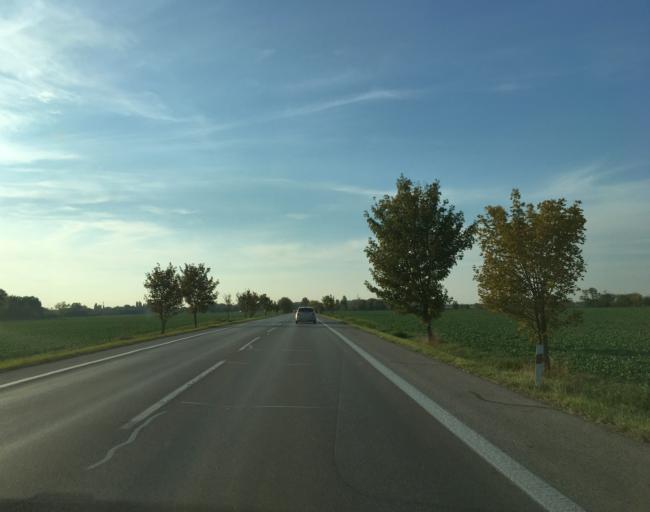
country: SK
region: Nitriansky
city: Sellye
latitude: 48.1500
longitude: 17.9556
